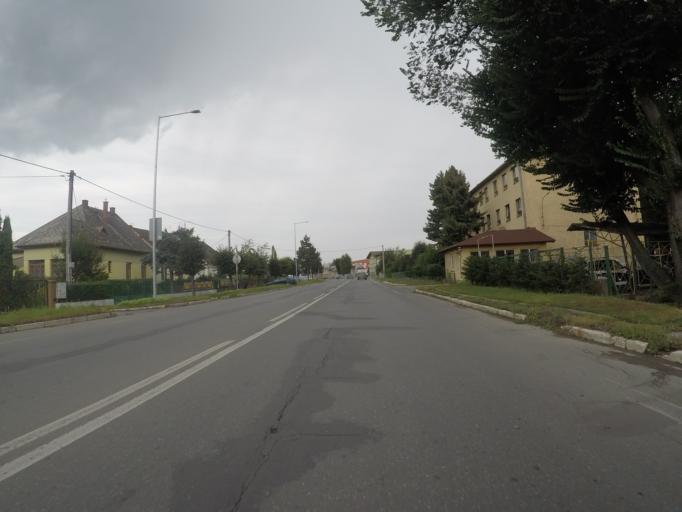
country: SK
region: Kosicky
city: Spisska Nova Ves
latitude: 48.9500
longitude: 20.5505
